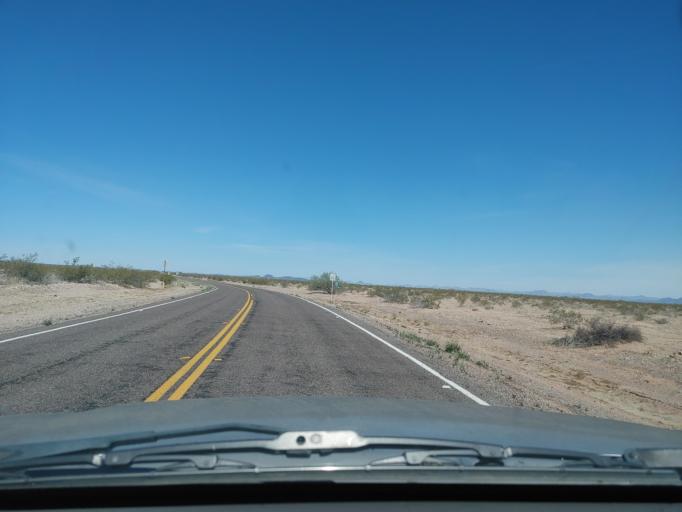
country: US
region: Arizona
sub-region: Maricopa County
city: Gila Bend
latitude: 32.8727
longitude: -113.2142
